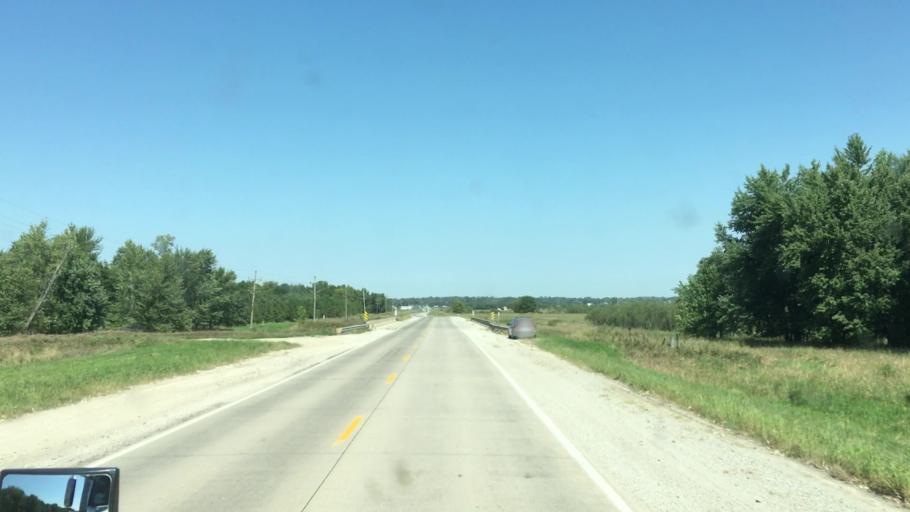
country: US
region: Iowa
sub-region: Benton County
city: Belle Plaine
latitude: 41.8661
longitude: -92.2778
